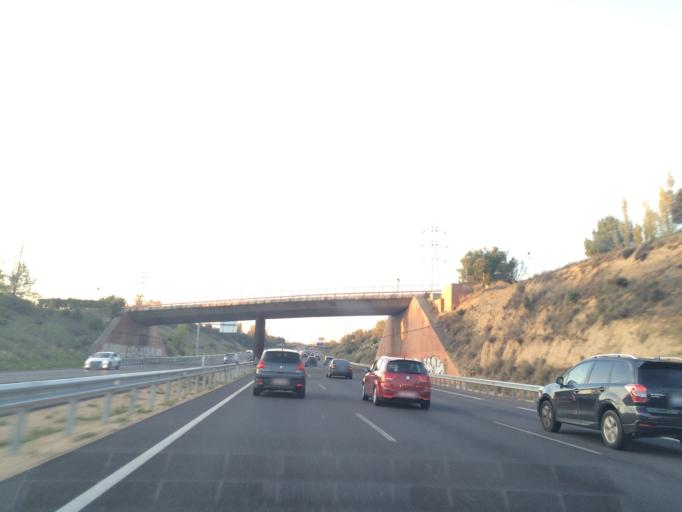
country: ES
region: Madrid
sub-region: Provincia de Madrid
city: Pozuelo de Alarcon
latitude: 40.4403
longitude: -3.8477
